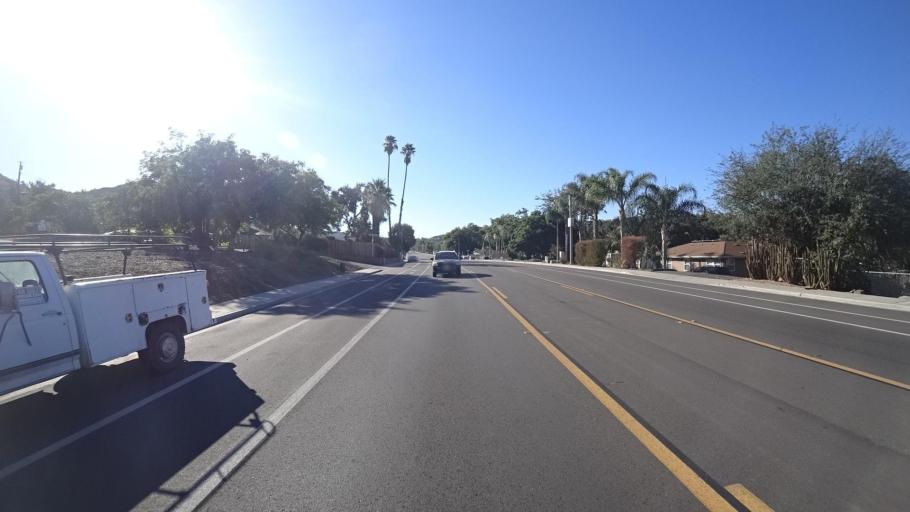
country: US
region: California
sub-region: San Diego County
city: Lakeside
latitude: 32.8525
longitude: -116.9187
